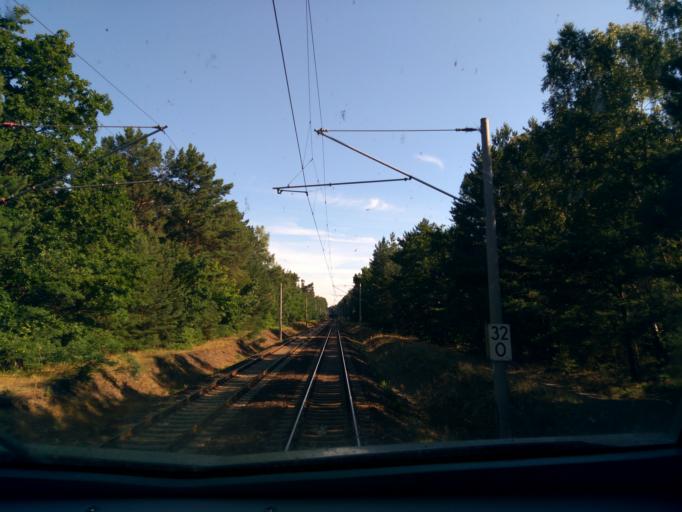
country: DE
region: Brandenburg
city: Bestensee
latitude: 52.2582
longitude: 13.6340
